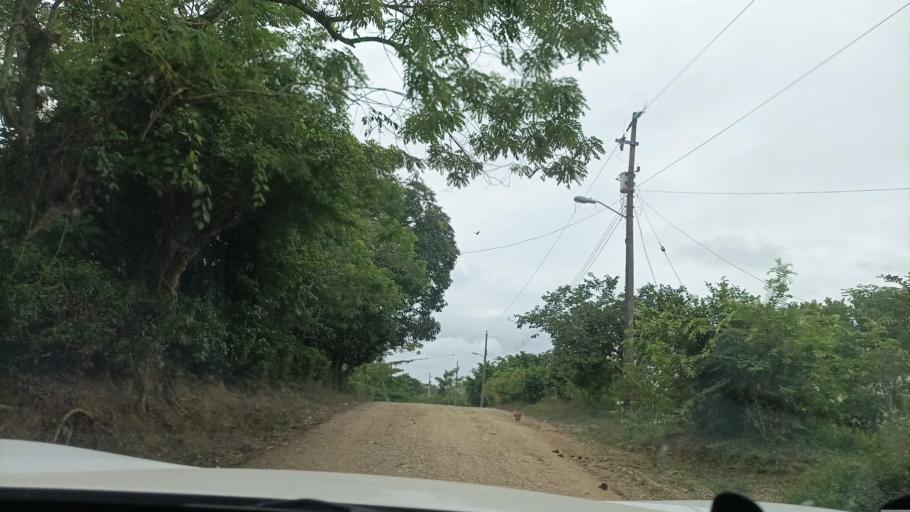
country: MX
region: Veracruz
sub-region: Uxpanapa
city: Poblado 10
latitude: 17.5551
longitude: -94.4274
